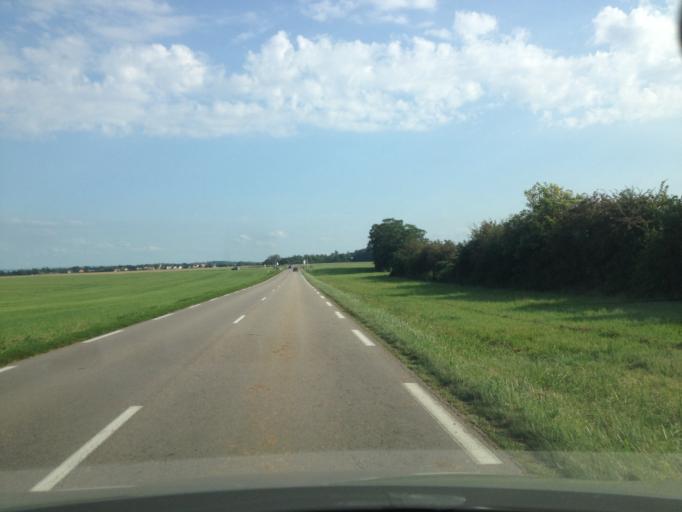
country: FR
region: Lower Normandy
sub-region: Departement du Calvados
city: Canon
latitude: 49.0709
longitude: -0.1323
